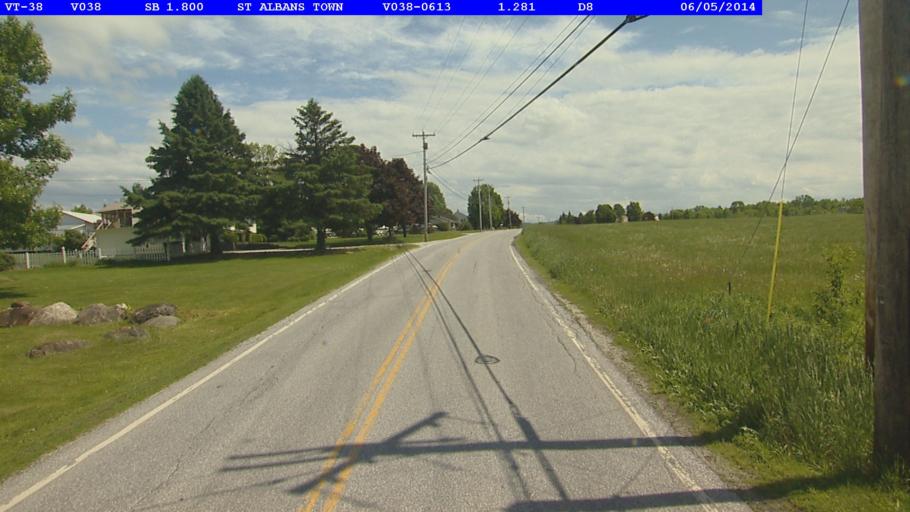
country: US
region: Vermont
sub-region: Franklin County
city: Saint Albans
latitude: 44.8398
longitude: -73.1024
